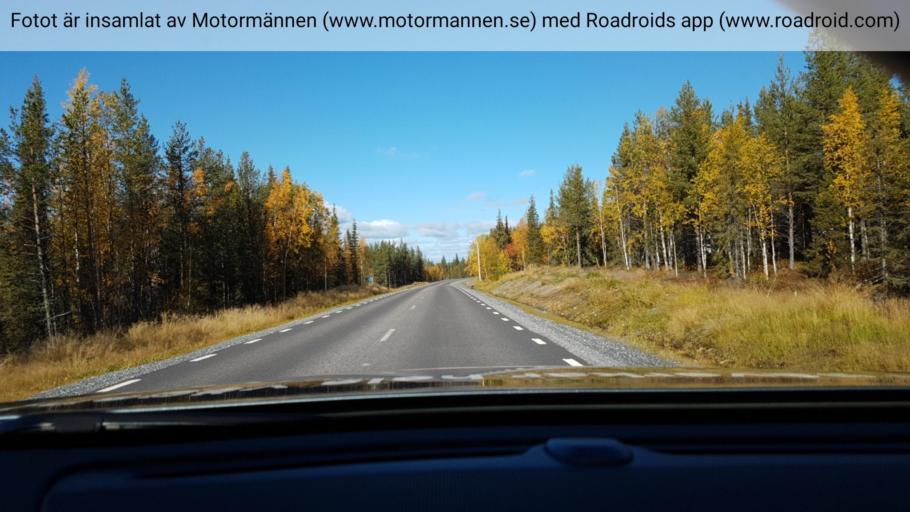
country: SE
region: Norrbotten
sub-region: Gallivare Kommun
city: Gaellivare
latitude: 67.0535
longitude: 20.7367
